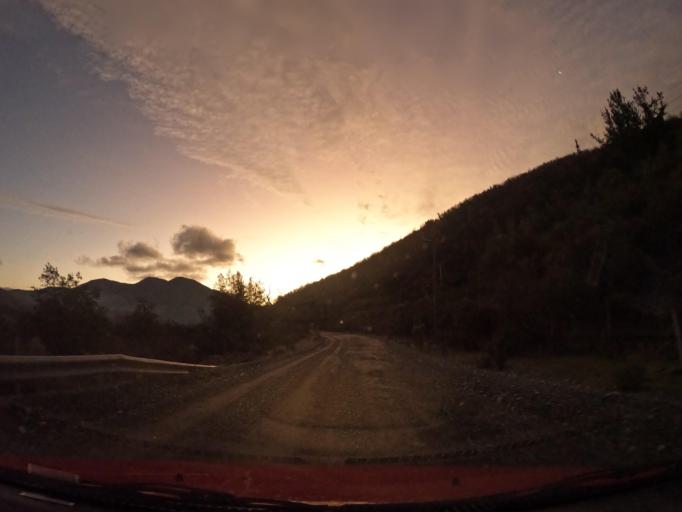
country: CL
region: Maule
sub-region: Provincia de Linares
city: Colbun
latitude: -35.8587
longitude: -71.2341
